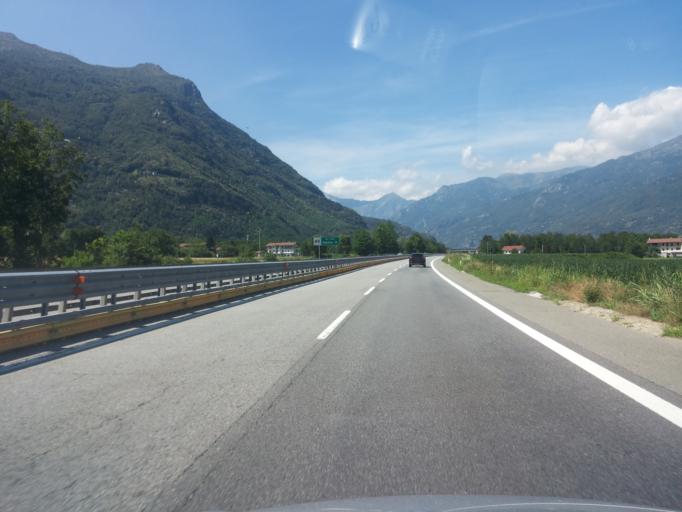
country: IT
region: Piedmont
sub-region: Provincia di Torino
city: Lessolo
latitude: 45.4906
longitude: 7.8305
